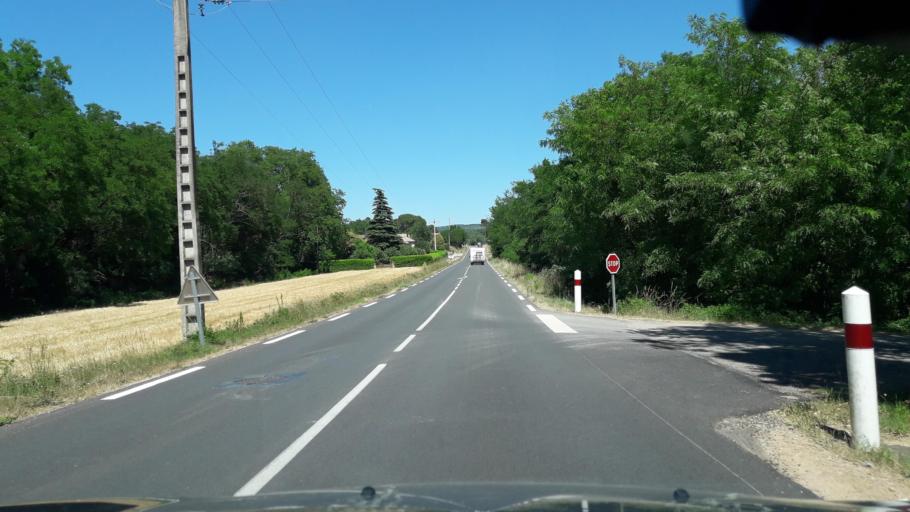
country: FR
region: Rhone-Alpes
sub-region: Departement de l'Ardeche
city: Ruoms
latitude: 44.4268
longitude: 4.3282
